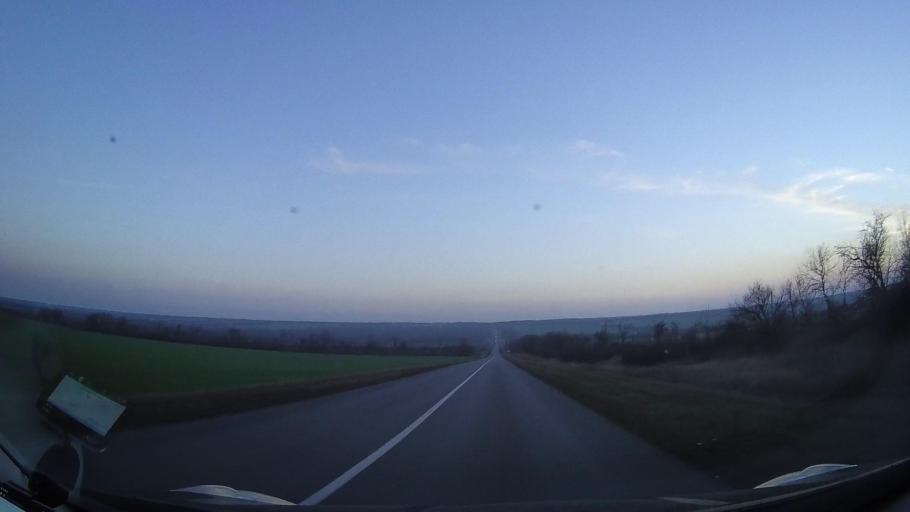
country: RU
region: Rostov
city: Zernograd
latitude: 46.9063
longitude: 40.3389
